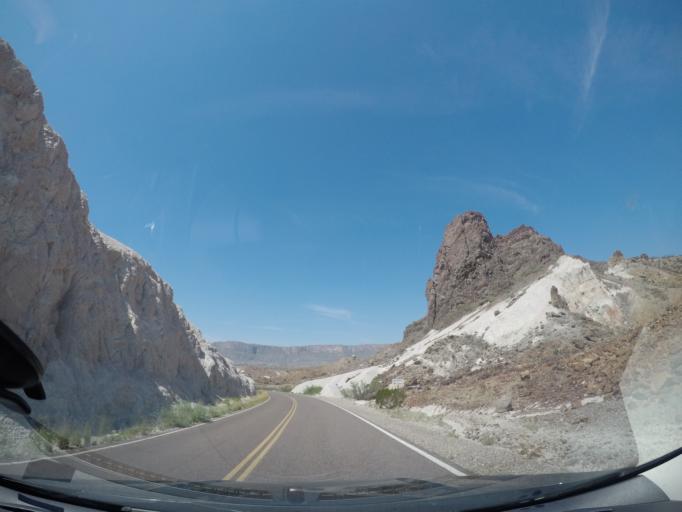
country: US
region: Texas
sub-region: Presidio County
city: Presidio
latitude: 29.1511
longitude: -103.5018
